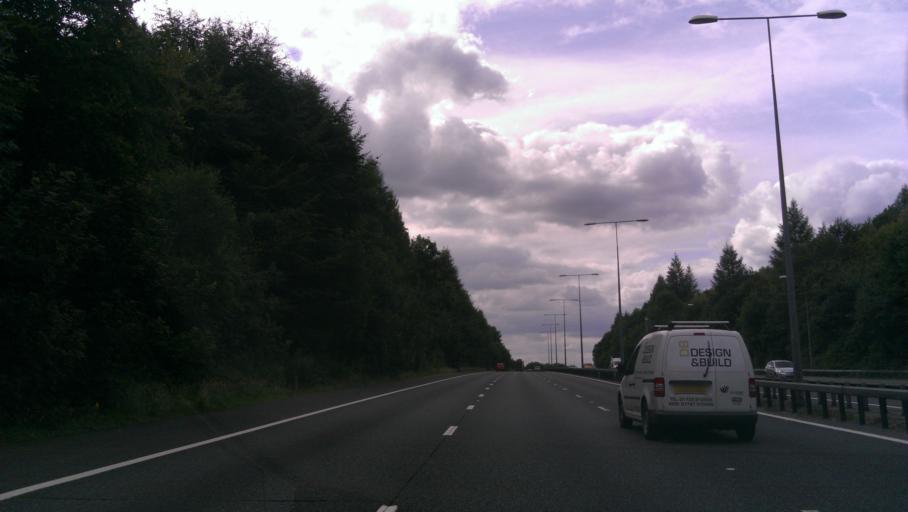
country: GB
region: England
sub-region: Kent
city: Borough Green
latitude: 51.3179
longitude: 0.2884
